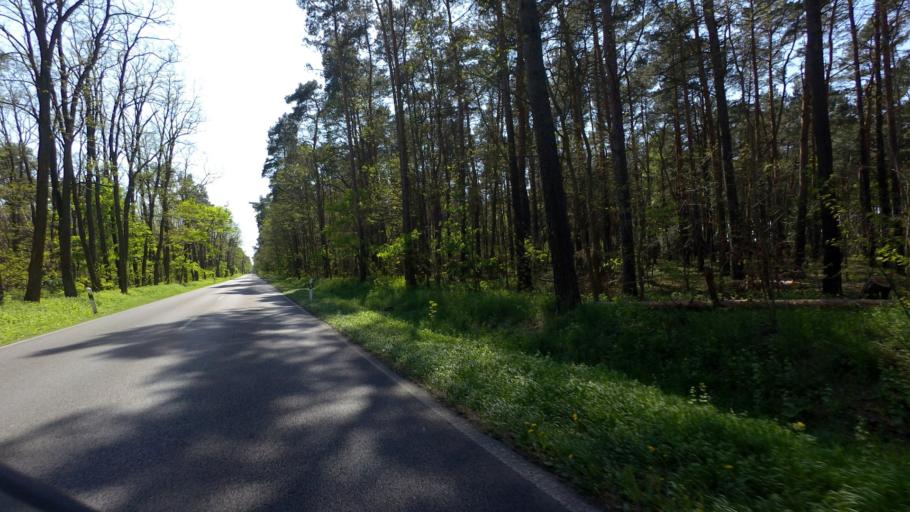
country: DE
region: Brandenburg
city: Tauche
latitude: 52.1292
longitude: 14.1983
